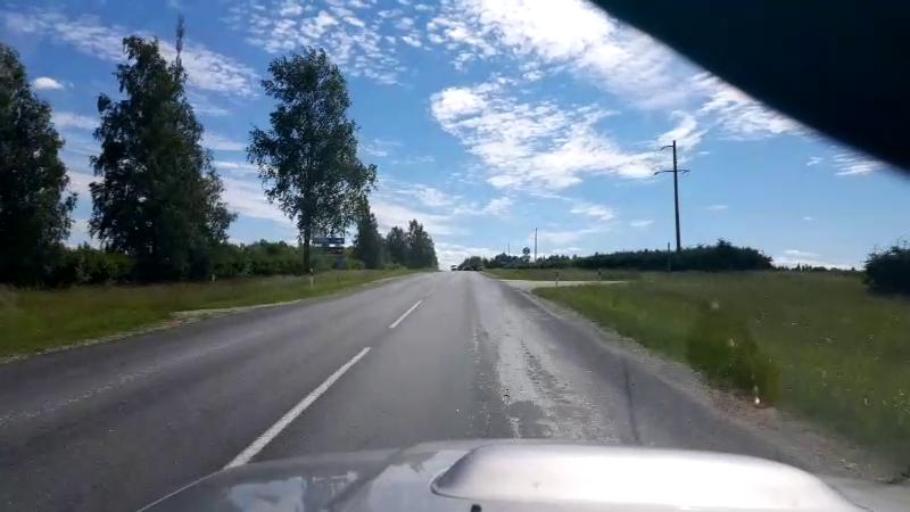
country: EE
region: Laeaene-Virumaa
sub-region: Rakke vald
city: Rakke
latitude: 58.8511
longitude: 26.2916
